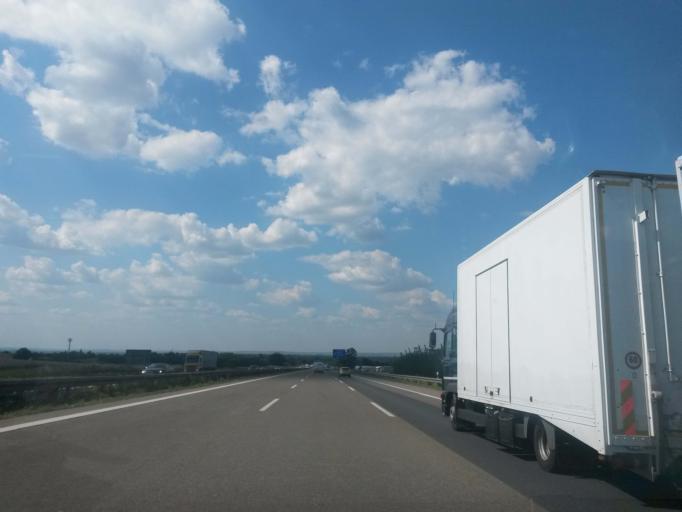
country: DE
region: Bavaria
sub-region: Upper Bavaria
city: Rohrbach
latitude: 48.6394
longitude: 11.5201
